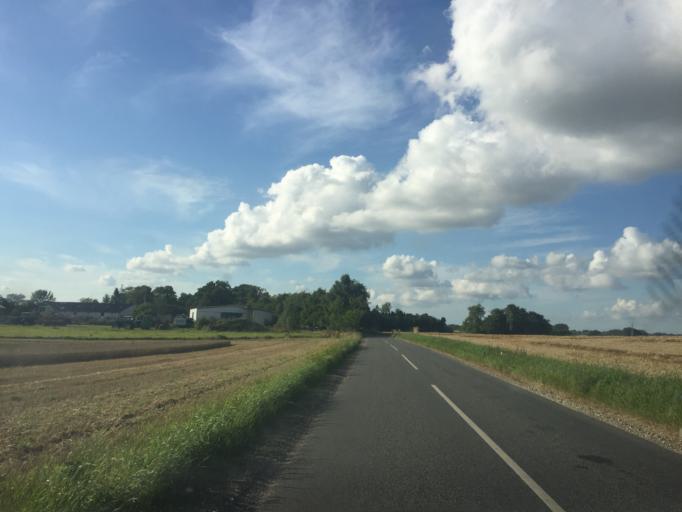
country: DK
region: Capital Region
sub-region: Egedal Kommune
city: Vekso
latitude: 55.7240
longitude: 12.2409
